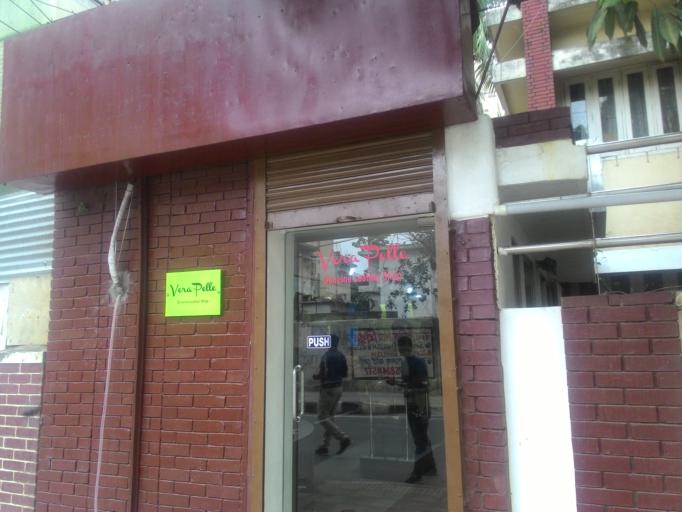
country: BD
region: Dhaka
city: Paltan
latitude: 23.7922
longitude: 90.4027
